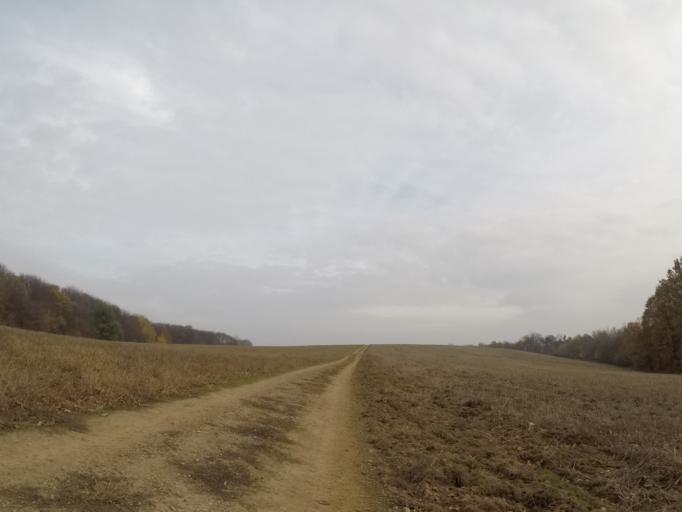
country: SK
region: Presovsky
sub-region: Okres Presov
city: Presov
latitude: 48.9406
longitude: 21.1485
